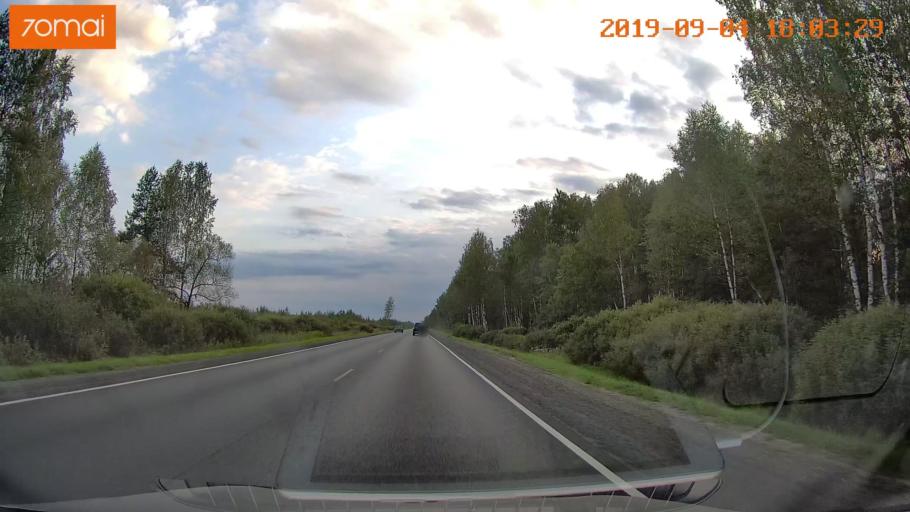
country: RU
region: Moskovskaya
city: Il'inskiy Pogost
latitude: 55.4629
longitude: 38.8515
